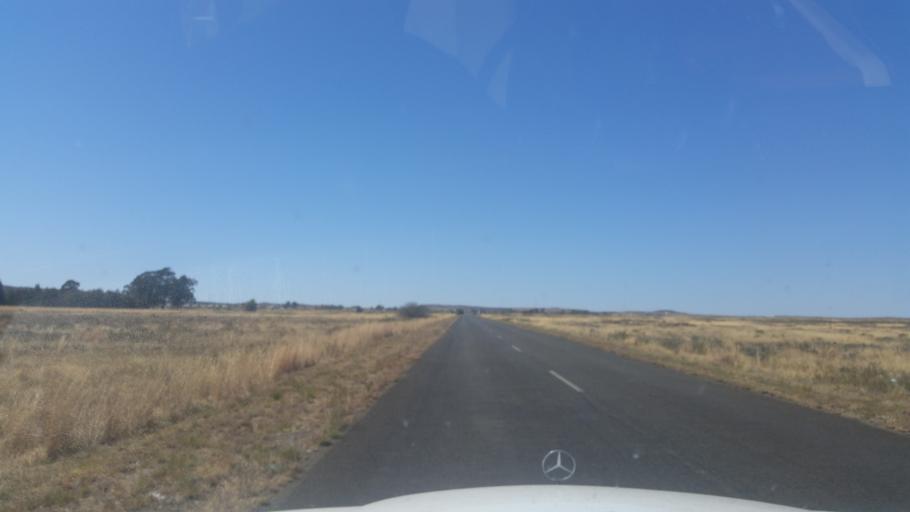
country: ZA
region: Eastern Cape
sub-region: Joe Gqabi District Municipality
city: Burgersdorp
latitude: -30.7601
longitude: 25.7812
